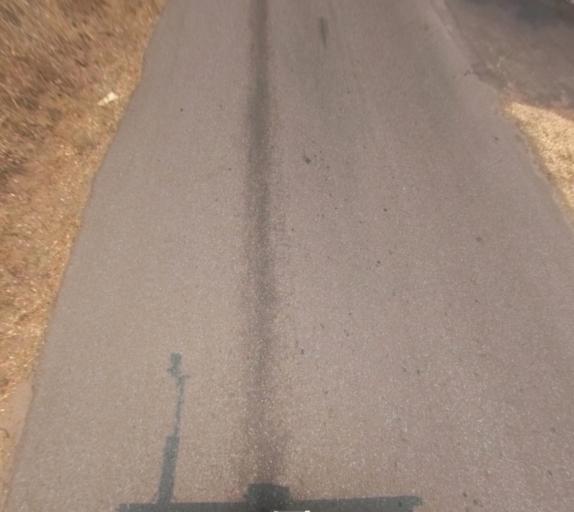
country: US
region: California
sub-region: Madera County
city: Oakhurst
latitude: 37.3369
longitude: -119.6541
